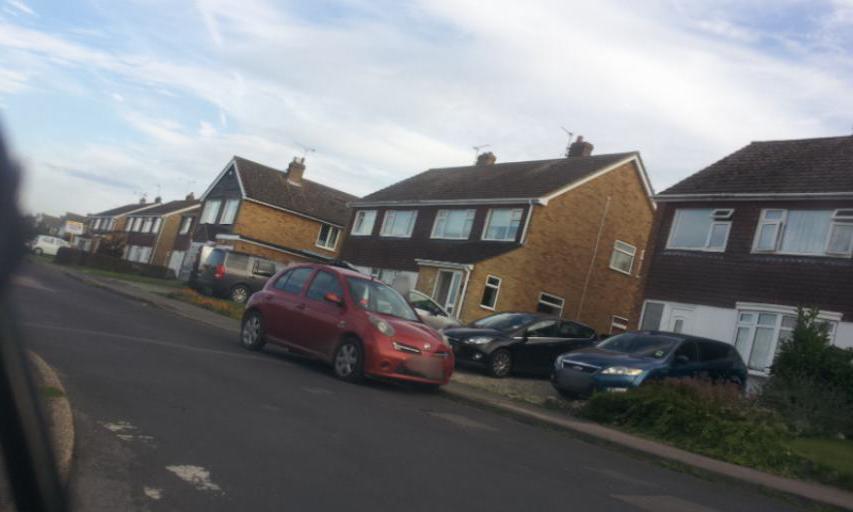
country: GB
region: England
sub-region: Kent
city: Maidstone
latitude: 51.2342
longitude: 0.4977
